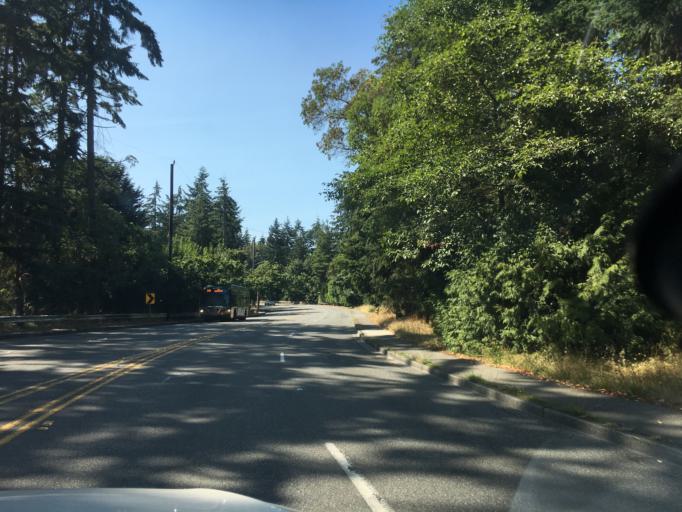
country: US
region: Washington
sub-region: King County
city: Shoreline
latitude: 47.7644
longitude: -122.3568
